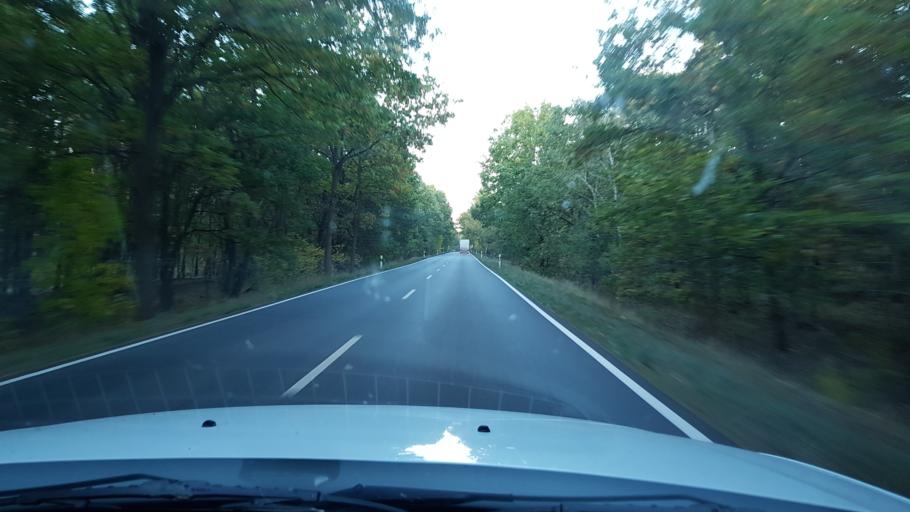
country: PL
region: West Pomeranian Voivodeship
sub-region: Powiat gryfinski
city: Widuchowa
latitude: 53.1574
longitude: 14.3276
